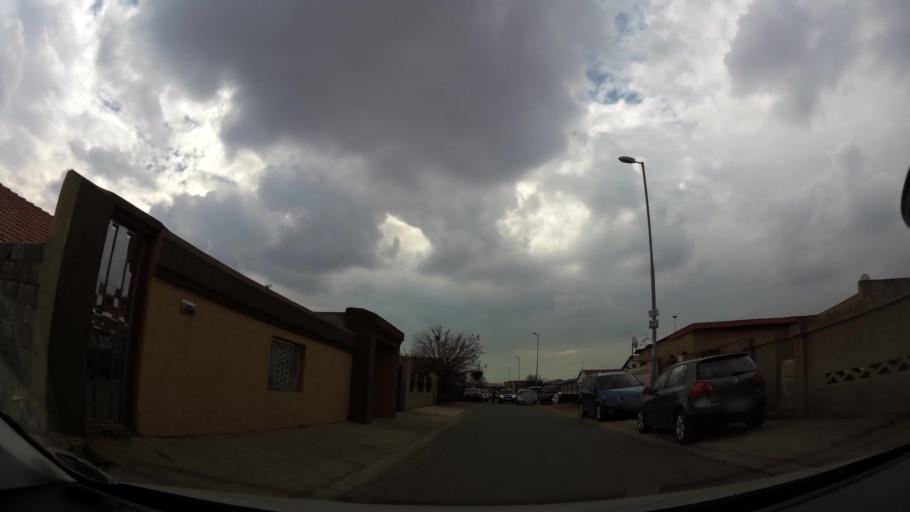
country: ZA
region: Gauteng
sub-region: City of Johannesburg Metropolitan Municipality
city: Soweto
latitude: -26.2617
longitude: 27.8561
